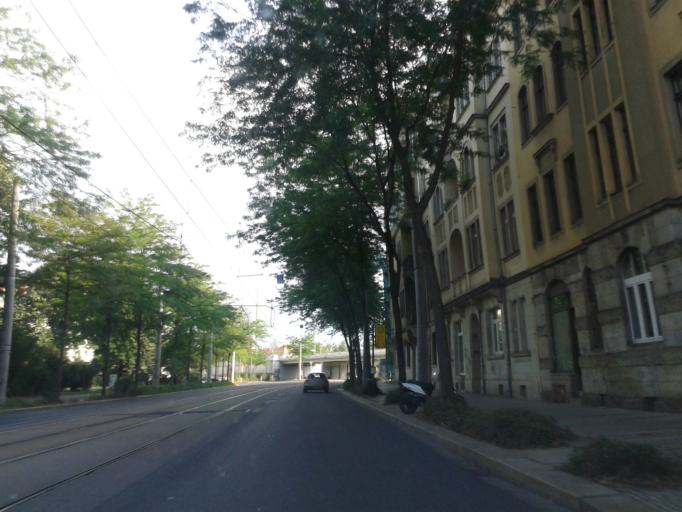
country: DE
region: Saxony
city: Dresden
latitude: 51.0792
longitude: 13.7321
